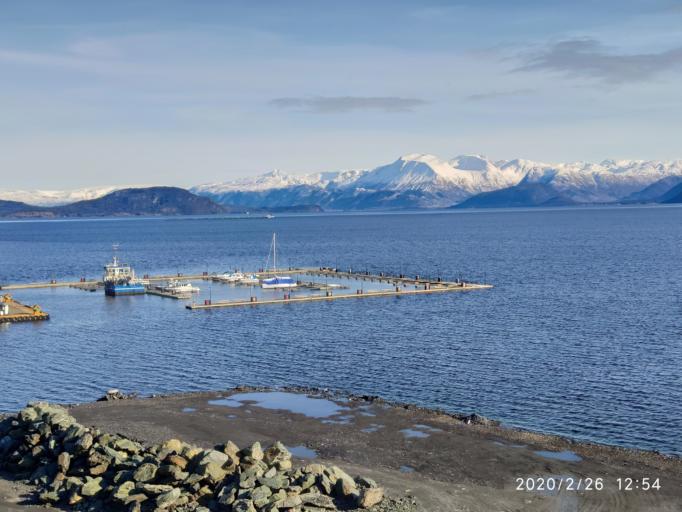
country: NO
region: Hordaland
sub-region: Tysnes
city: Uggdal
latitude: 59.9432
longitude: 5.6233
